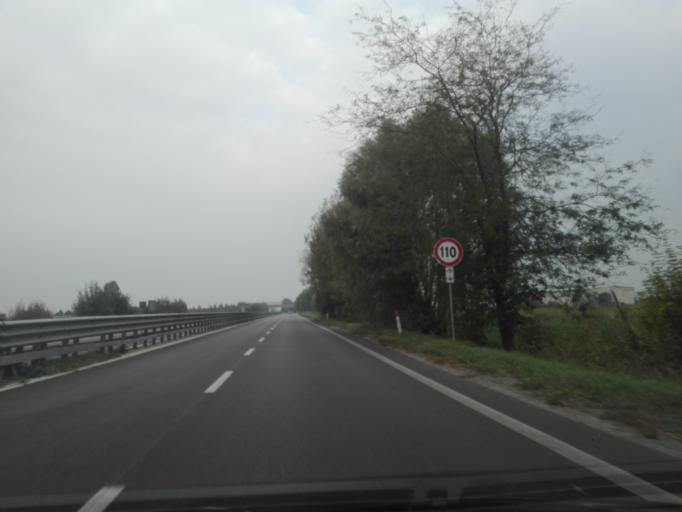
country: IT
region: Veneto
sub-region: Provincia di Verona
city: Villa Bartolomea
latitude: 45.1457
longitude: 11.3483
